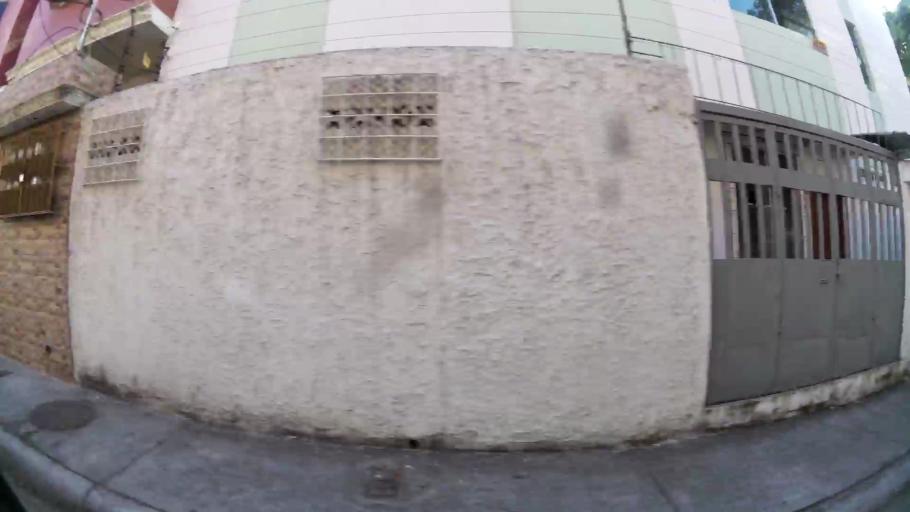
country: EC
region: Guayas
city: Guayaquil
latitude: -2.1696
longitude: -79.8959
